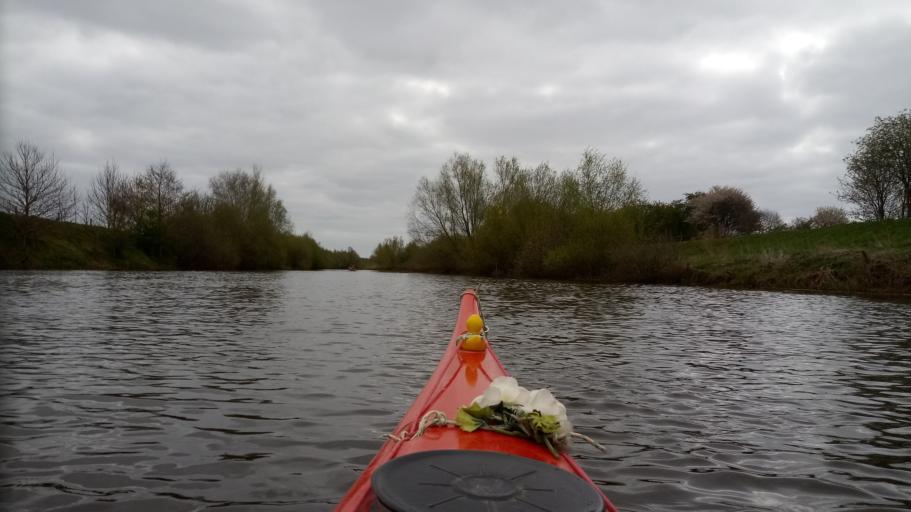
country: NL
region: Overijssel
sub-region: Gemeente Twenterand
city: Den Ham
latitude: 52.5040
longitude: 6.4017
